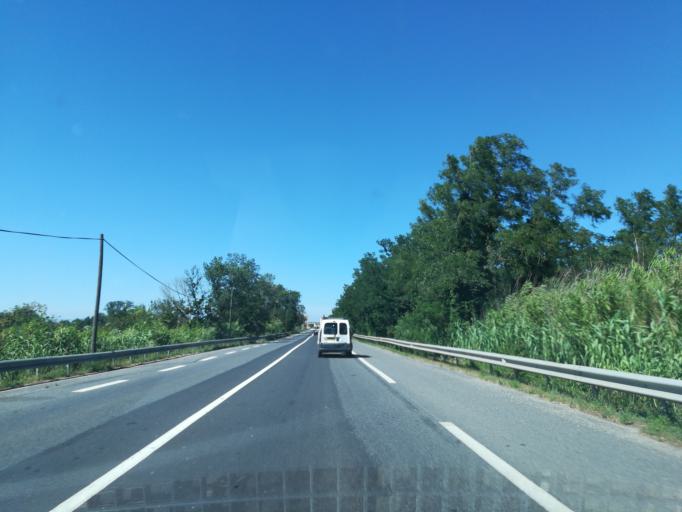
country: FR
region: Languedoc-Roussillon
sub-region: Departement des Pyrenees-Orientales
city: Villemolaque
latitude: 42.6048
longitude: 2.8586
